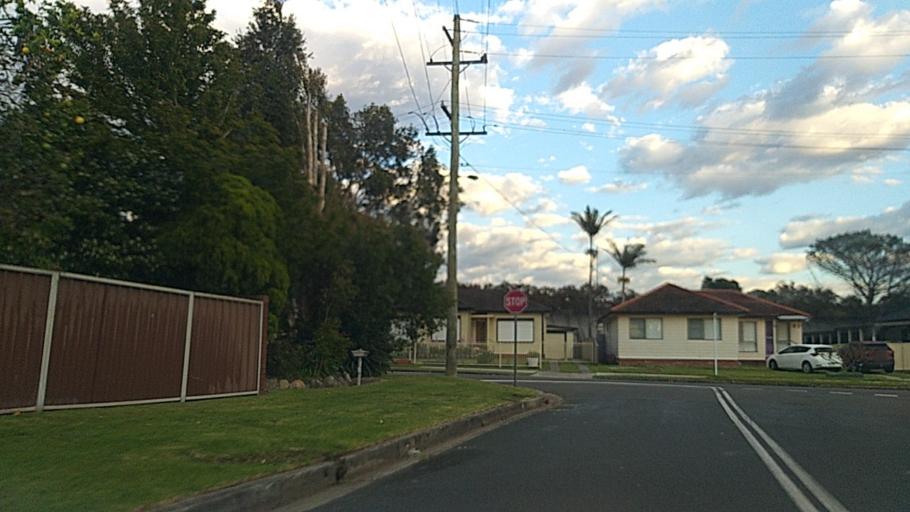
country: AU
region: New South Wales
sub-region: Wollongong
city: Koonawarra
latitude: -34.4990
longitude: 150.7983
